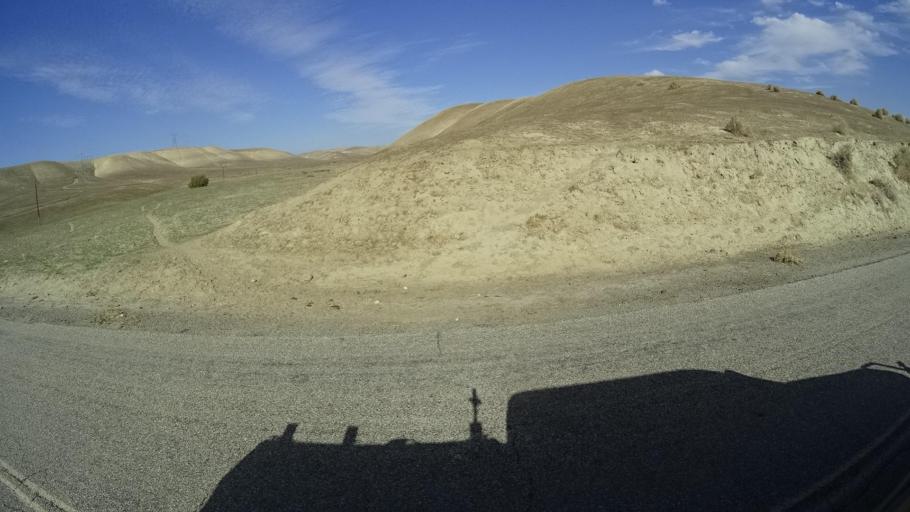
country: US
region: California
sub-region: Kern County
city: Oildale
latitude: 35.5185
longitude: -118.9174
